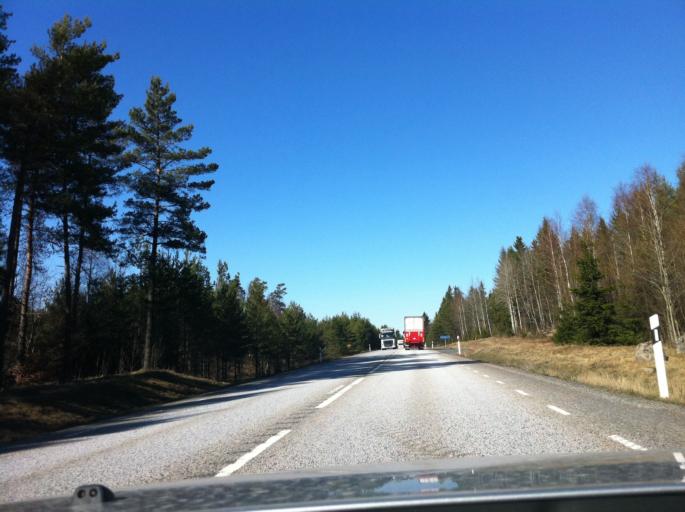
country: SE
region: Joenkoeping
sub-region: Mullsjo Kommun
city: Mullsjoe
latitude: 57.9613
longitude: 13.8321
